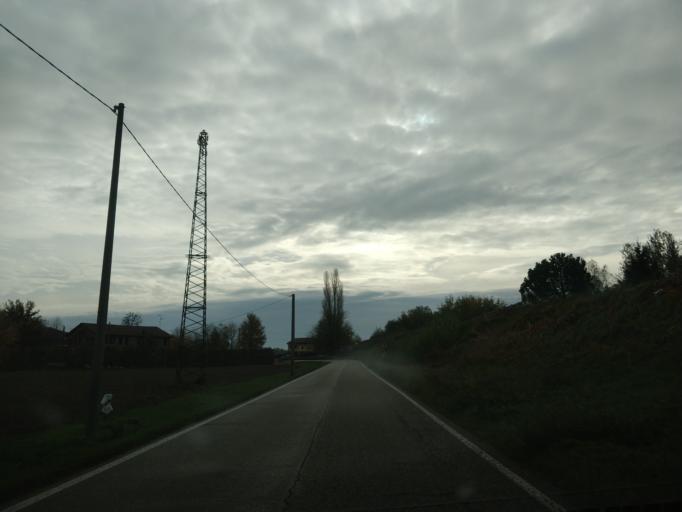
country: IT
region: Emilia-Romagna
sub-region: Provincia di Bologna
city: Argelato
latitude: 44.6204
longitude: 11.3162
